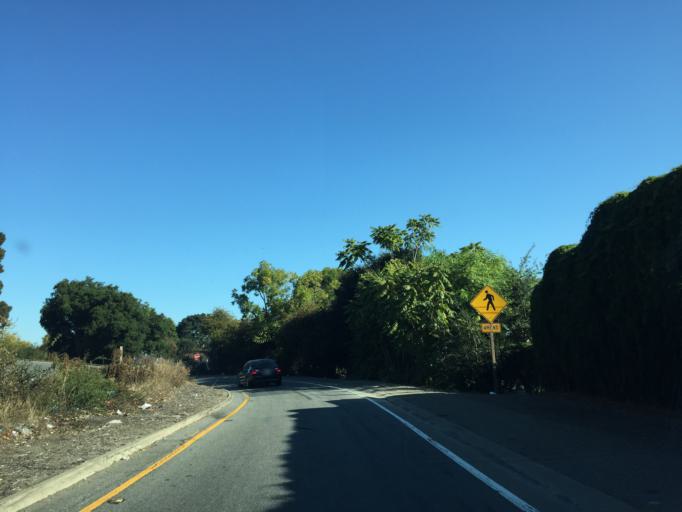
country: US
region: California
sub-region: San Mateo County
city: East Palo Alto
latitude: 37.4689
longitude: -122.1540
